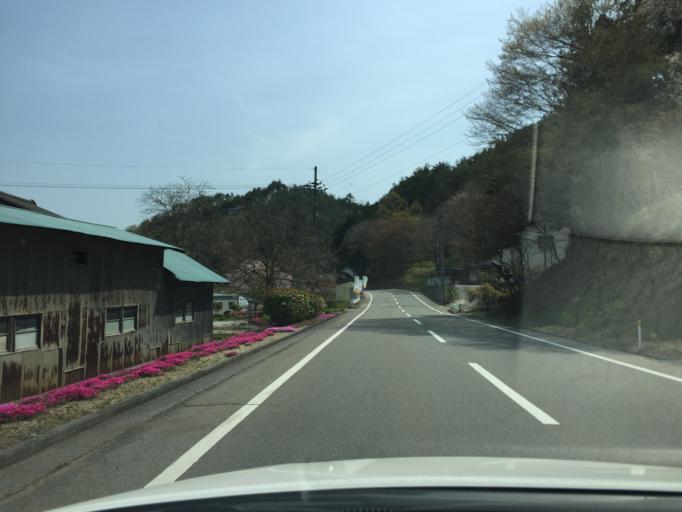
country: JP
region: Fukushima
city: Iwaki
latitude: 37.2928
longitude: 140.8375
